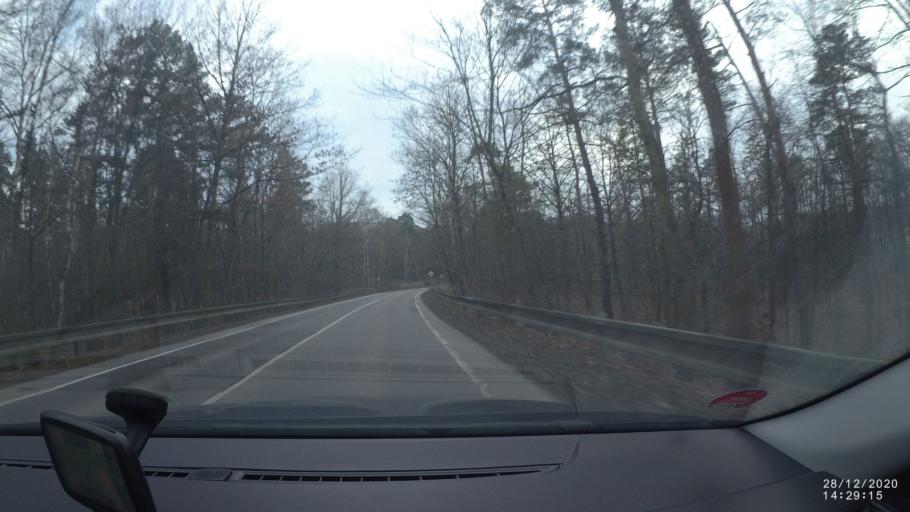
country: CZ
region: Central Bohemia
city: Sestajovice
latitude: 50.0868
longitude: 14.6662
